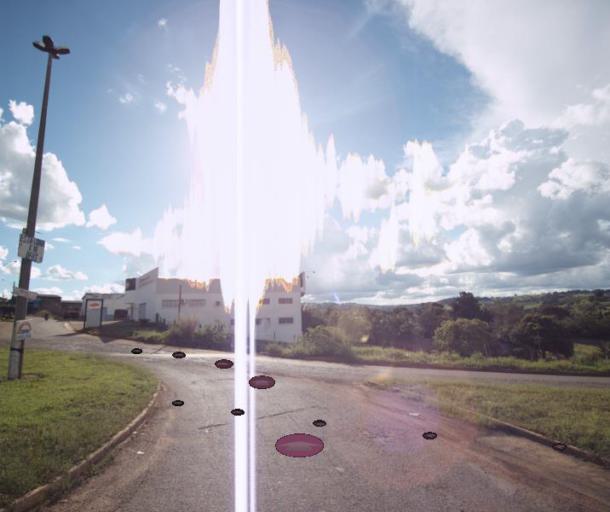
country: BR
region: Goias
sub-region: Rialma
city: Rialma
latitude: -15.3099
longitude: -49.5720
